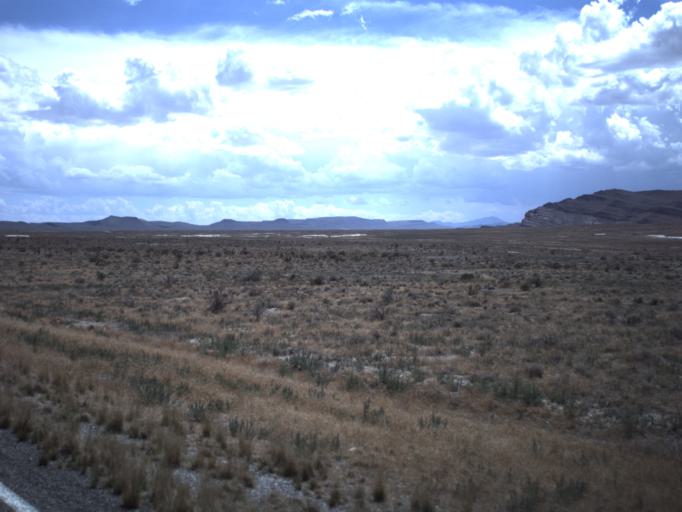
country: US
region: Utah
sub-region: Beaver County
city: Milford
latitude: 39.0386
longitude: -113.3970
